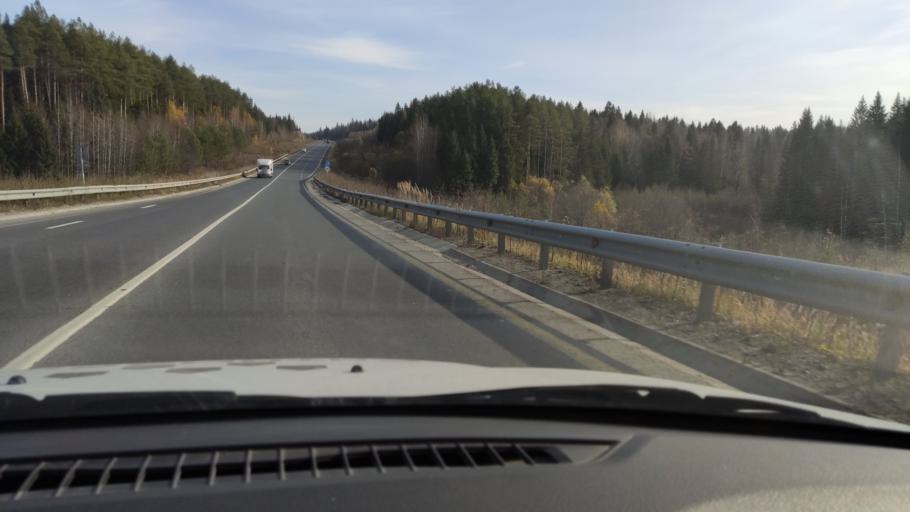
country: RU
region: Perm
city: Novyye Lyady
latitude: 58.0366
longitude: 56.4713
